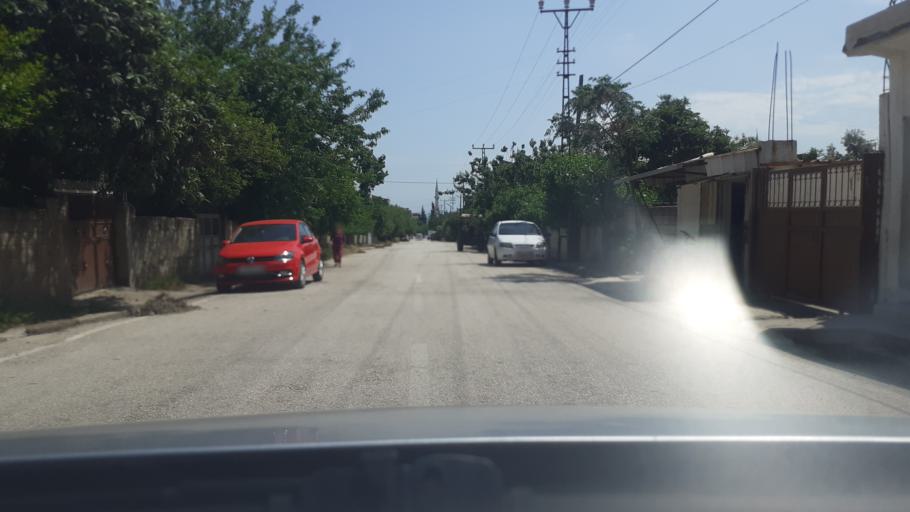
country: TR
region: Hatay
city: Kirikhan
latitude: 36.4906
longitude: 36.3540
